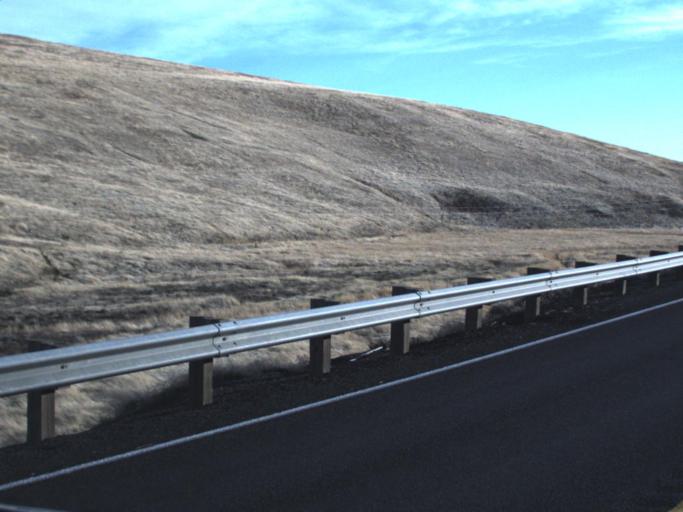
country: US
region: Washington
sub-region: Columbia County
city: Dayton
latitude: 46.4741
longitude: -117.9617
